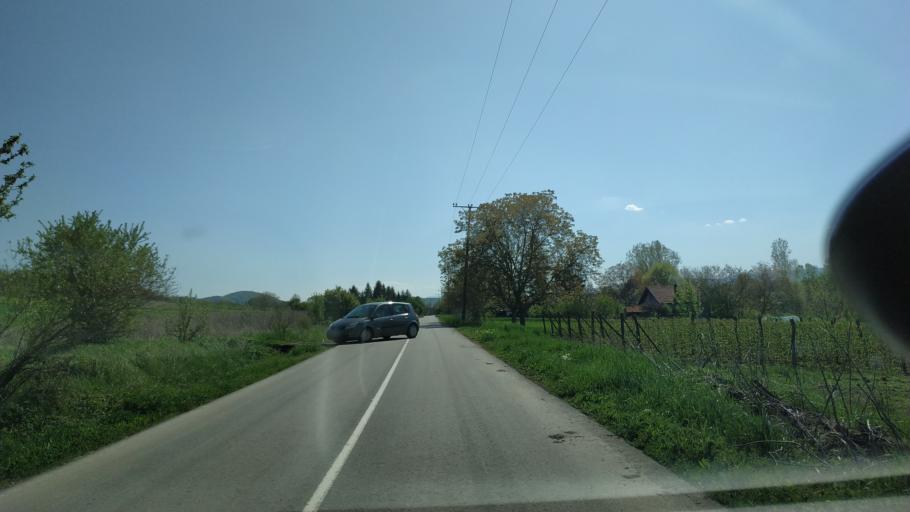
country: RS
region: Central Serbia
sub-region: Nisavski Okrug
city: Nis
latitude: 43.4583
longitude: 21.8547
